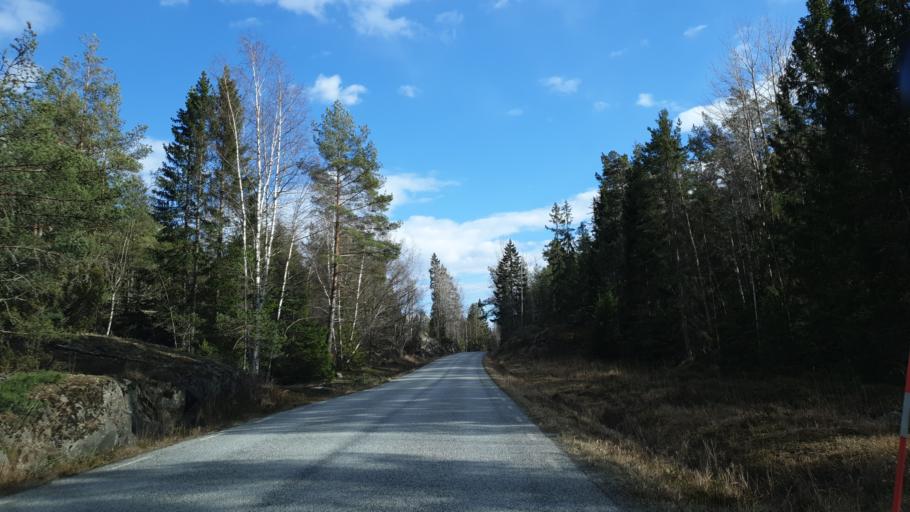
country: SE
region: Stockholm
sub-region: Varmdo Kommun
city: Mortnas
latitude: 59.2441
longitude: 18.4674
